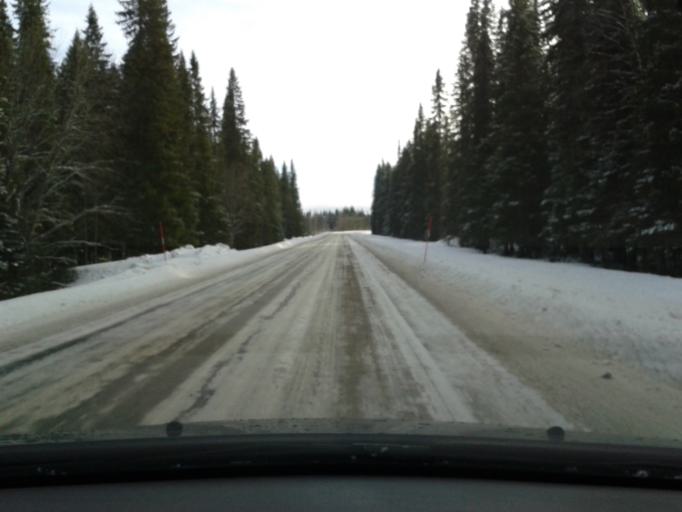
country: SE
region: Vaesterbotten
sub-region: Vilhelmina Kommun
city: Sjoberg
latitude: 64.7376
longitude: 16.2105
